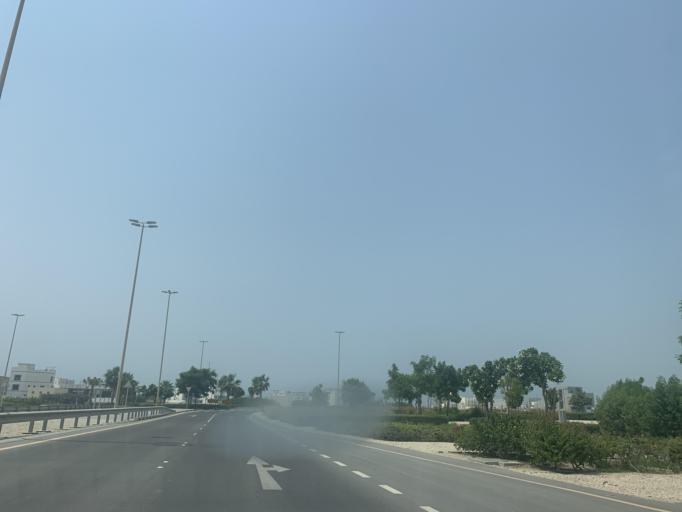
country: BH
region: Muharraq
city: Al Muharraq
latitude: 26.3179
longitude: 50.6255
